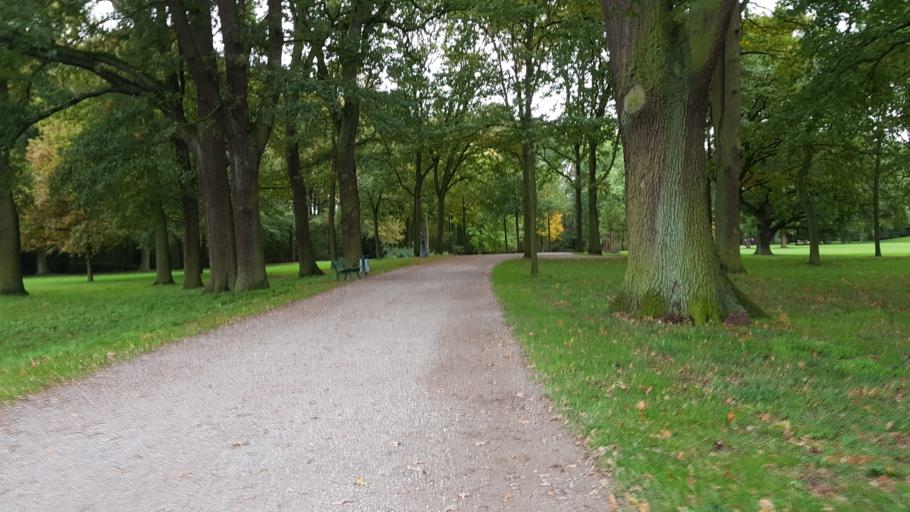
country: DE
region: Bremen
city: Bremen
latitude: 53.0911
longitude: 8.8245
